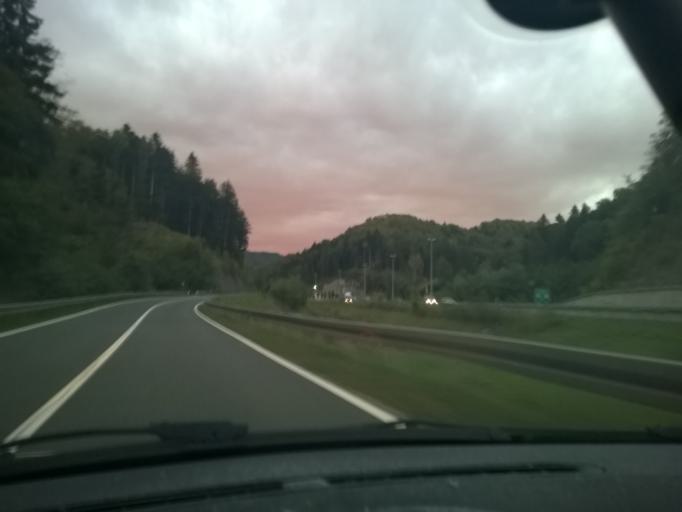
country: SI
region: Zetale
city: Zetale
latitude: 46.2359
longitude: 15.8457
